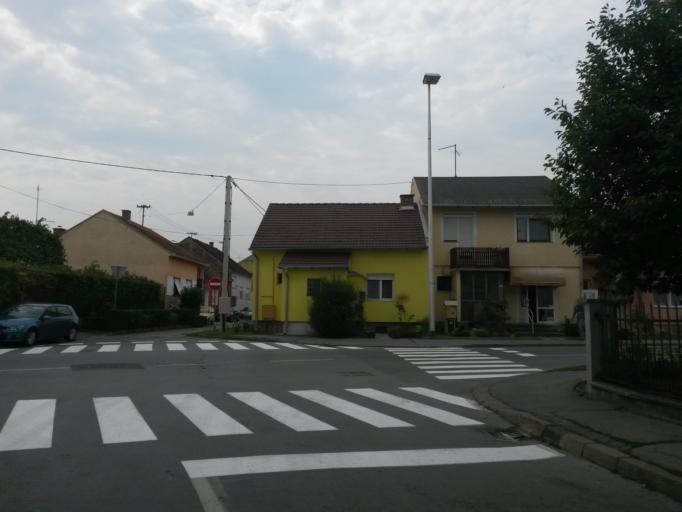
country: HR
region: Osjecko-Baranjska
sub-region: Grad Osijek
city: Osijek
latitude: 45.5464
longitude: 18.7164
